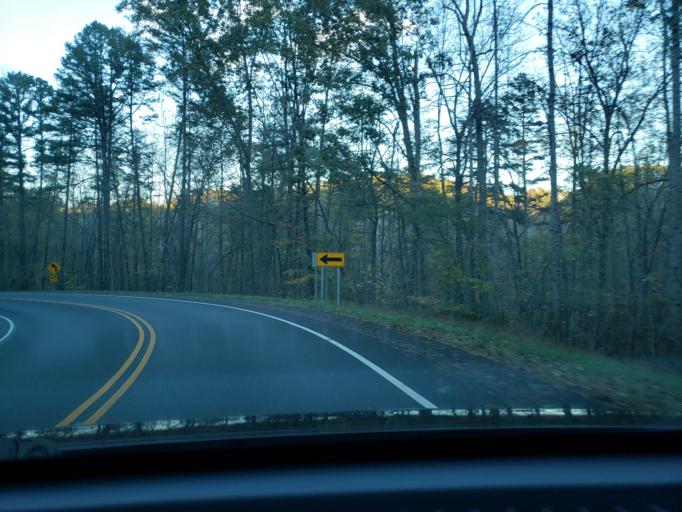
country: US
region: North Carolina
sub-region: Stokes County
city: Danbury
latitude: 36.3801
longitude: -80.1862
